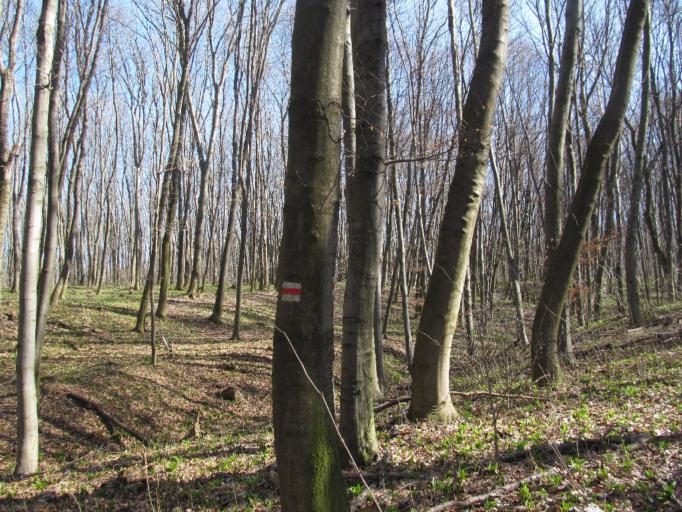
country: HU
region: Fejer
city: Bakonycsernye
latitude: 47.2808
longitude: 18.0836
